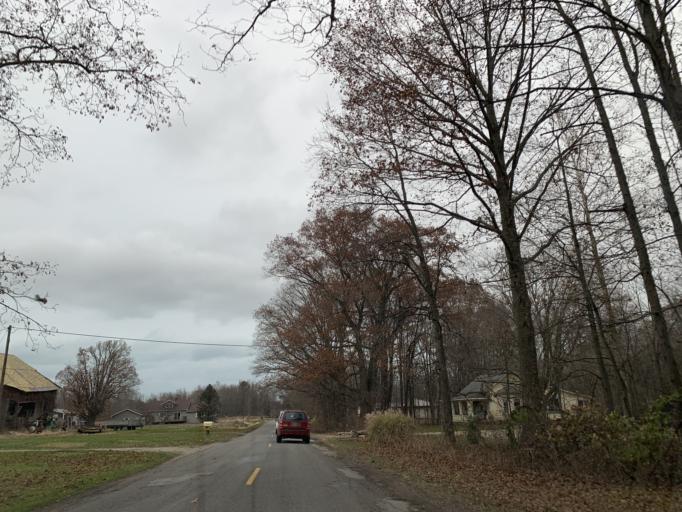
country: US
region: Michigan
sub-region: Berrien County
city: Three Oaks
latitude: 41.8062
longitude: -86.6684
